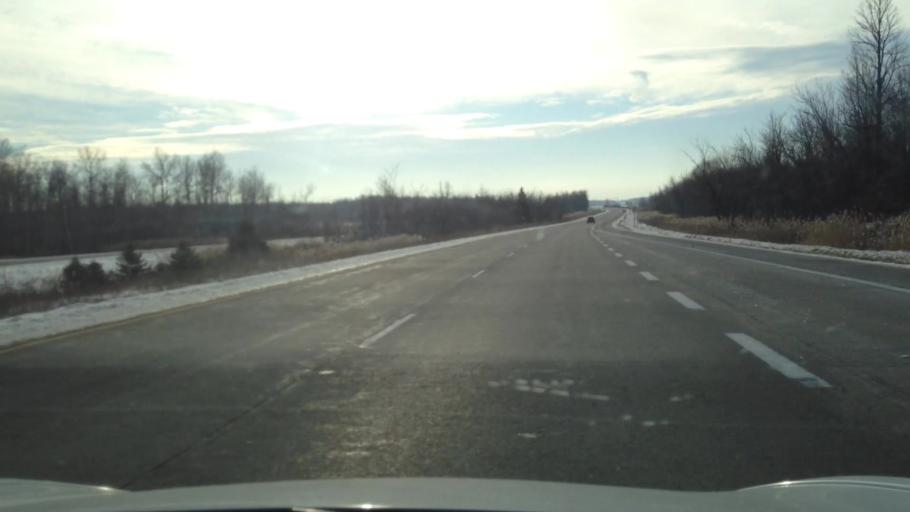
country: CA
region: Ontario
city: Hawkesbury
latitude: 45.4334
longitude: -74.7462
